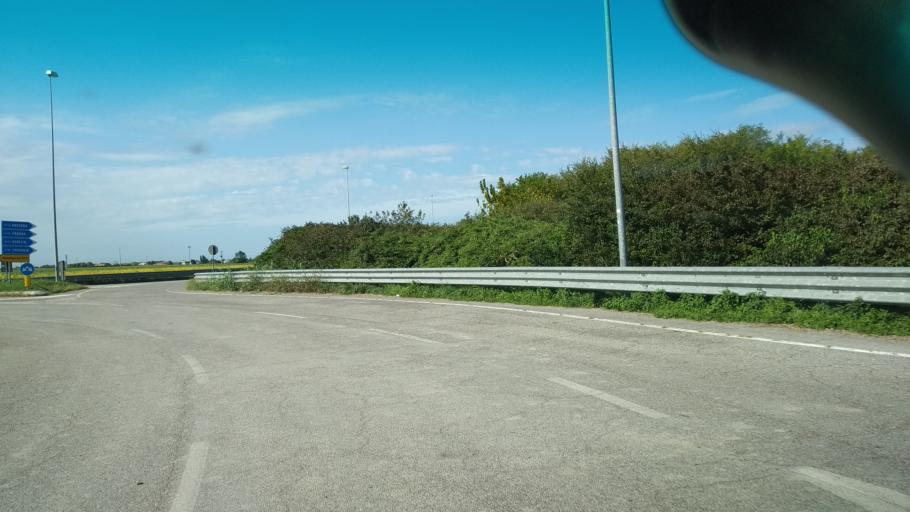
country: IT
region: Veneto
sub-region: Provincia di Venezia
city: Valli
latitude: 45.2241
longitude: 12.1770
